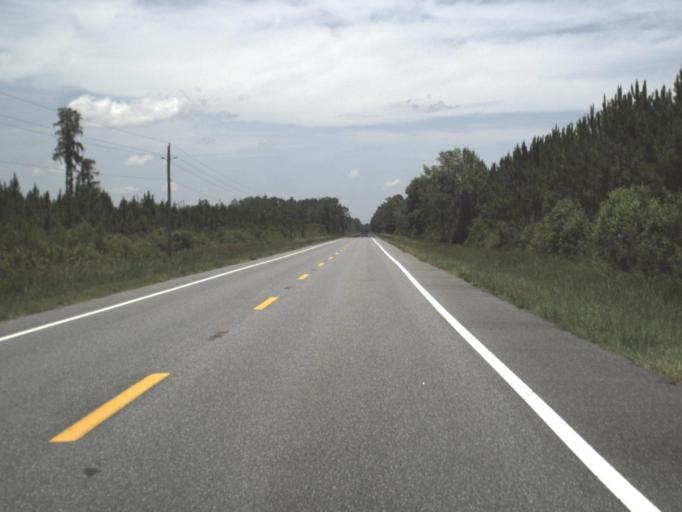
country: US
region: Florida
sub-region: Lafayette County
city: Mayo
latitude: 29.9927
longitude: -83.1966
